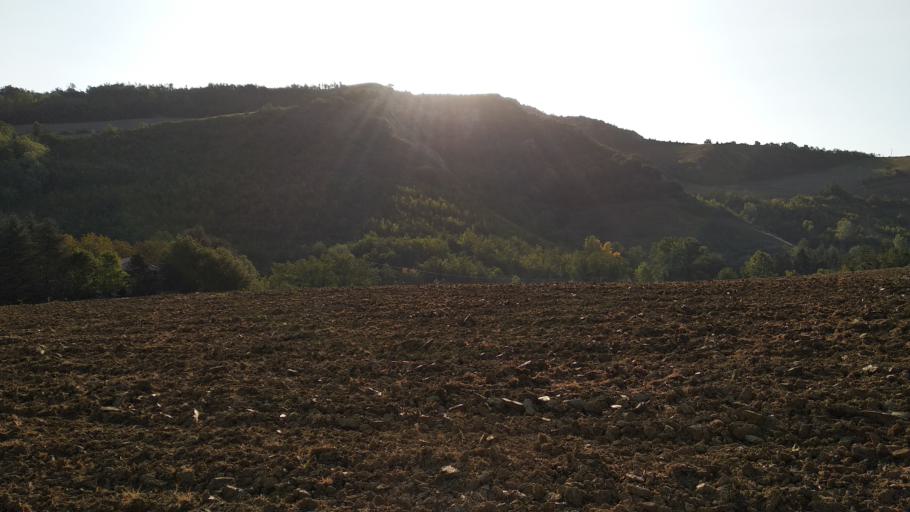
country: IT
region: Emilia-Romagna
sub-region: Provincia di Bologna
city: Borgo Tossignano
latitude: 44.3257
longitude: 11.5748
